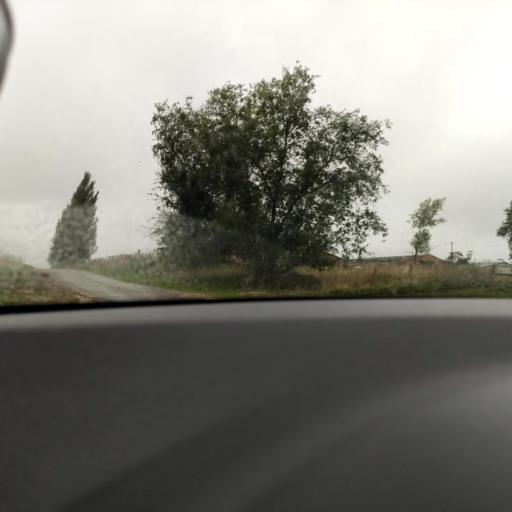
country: RU
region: Samara
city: Yelkhovka
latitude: 53.7458
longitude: 50.2437
